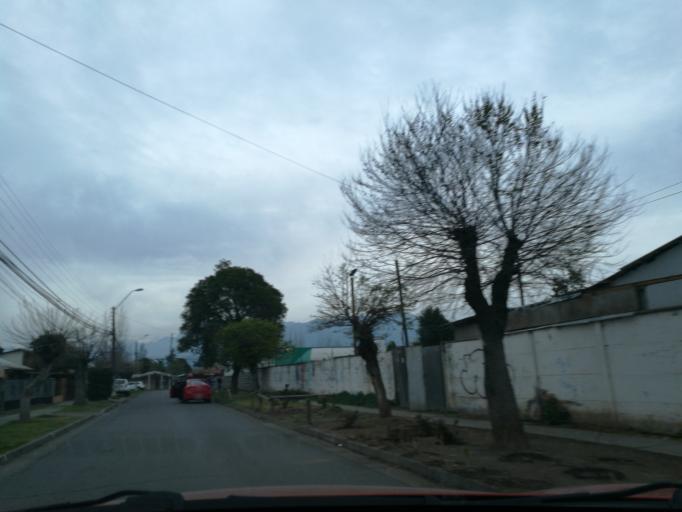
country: CL
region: O'Higgins
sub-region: Provincia de Cachapoal
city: Machali
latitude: -34.1766
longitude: -70.6901
